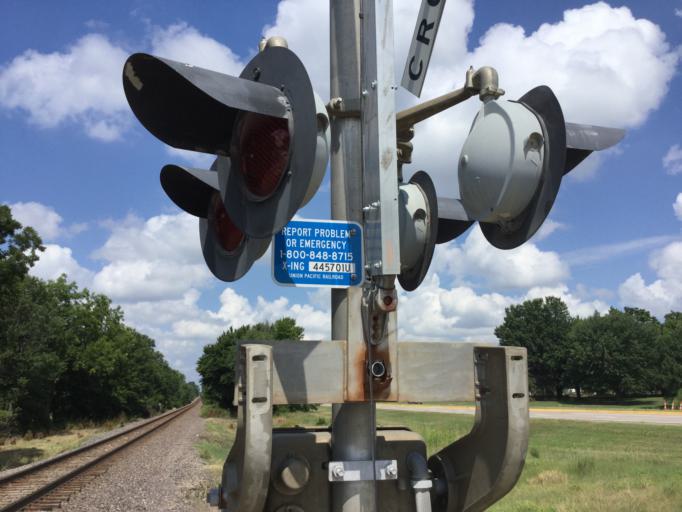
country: US
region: Kansas
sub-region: Montgomery County
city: Coffeyville
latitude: 37.0334
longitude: -95.6565
